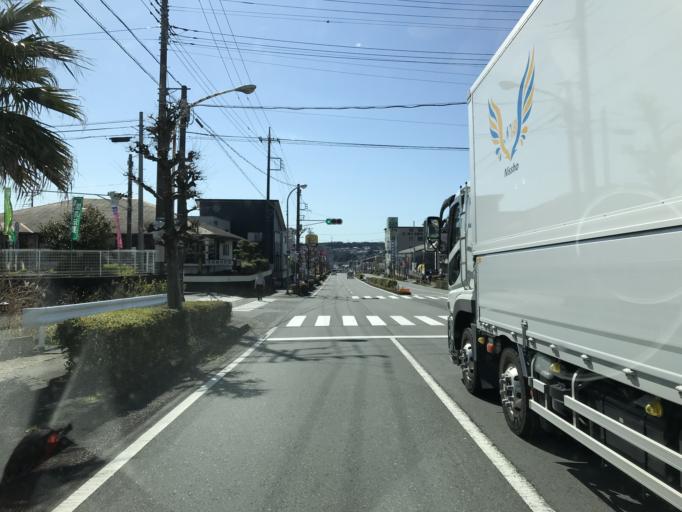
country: JP
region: Shizuoka
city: Fujinomiya
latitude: 35.2209
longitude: 138.6284
